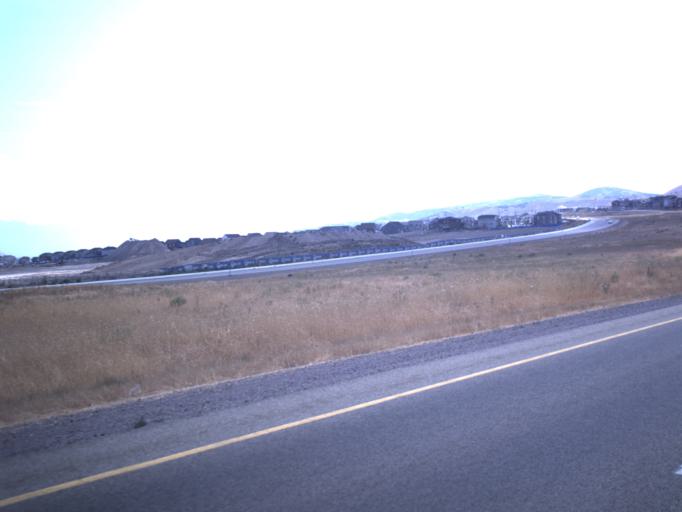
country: US
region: Utah
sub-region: Salt Lake County
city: Herriman
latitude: 40.4979
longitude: -112.0051
